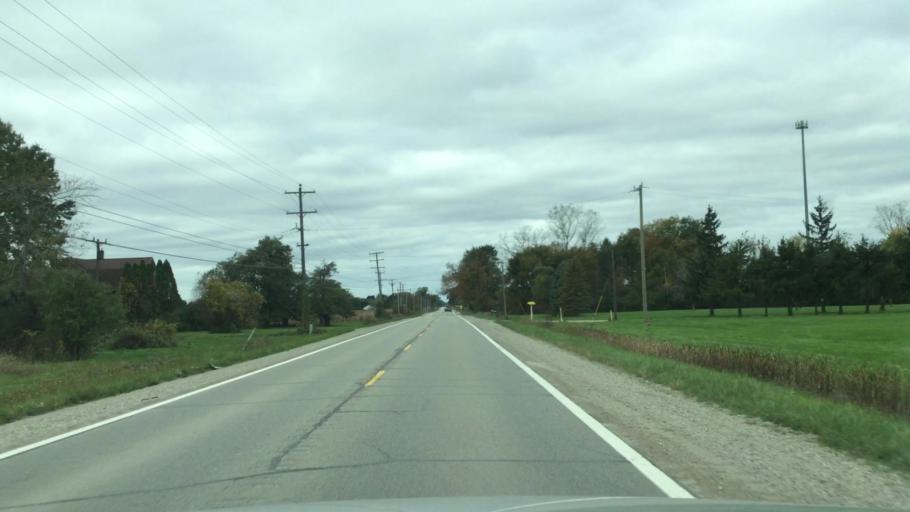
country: US
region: Michigan
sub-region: Macomb County
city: Armada
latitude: 42.8076
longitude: -82.8271
